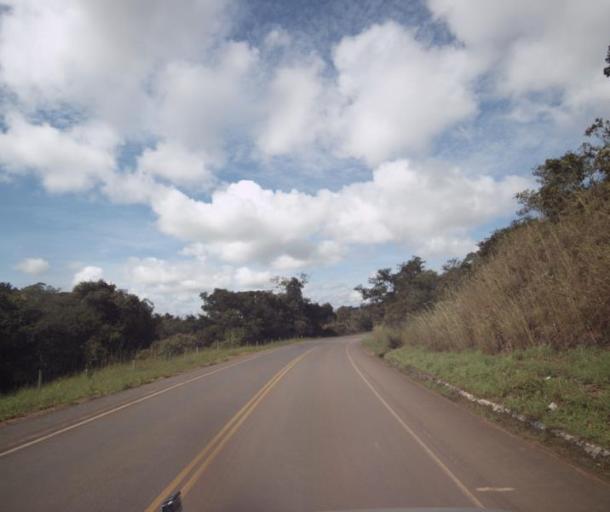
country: BR
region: Goias
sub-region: Pirenopolis
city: Pirenopolis
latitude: -15.9373
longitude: -48.8051
